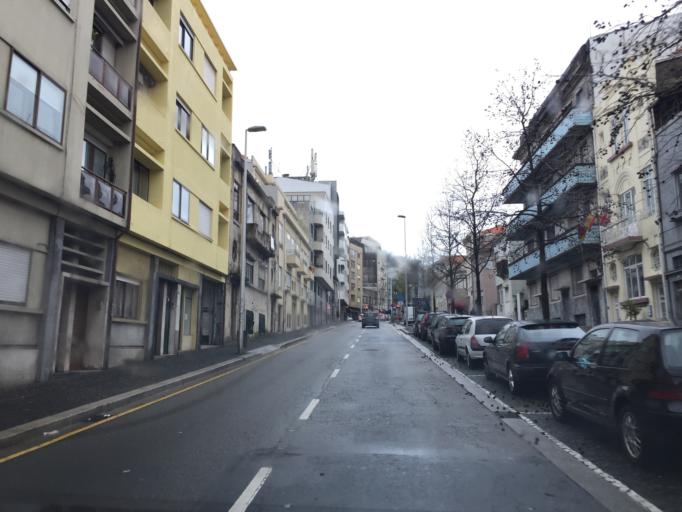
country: PT
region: Porto
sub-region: Porto
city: Porto
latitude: 41.1561
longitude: -8.6092
